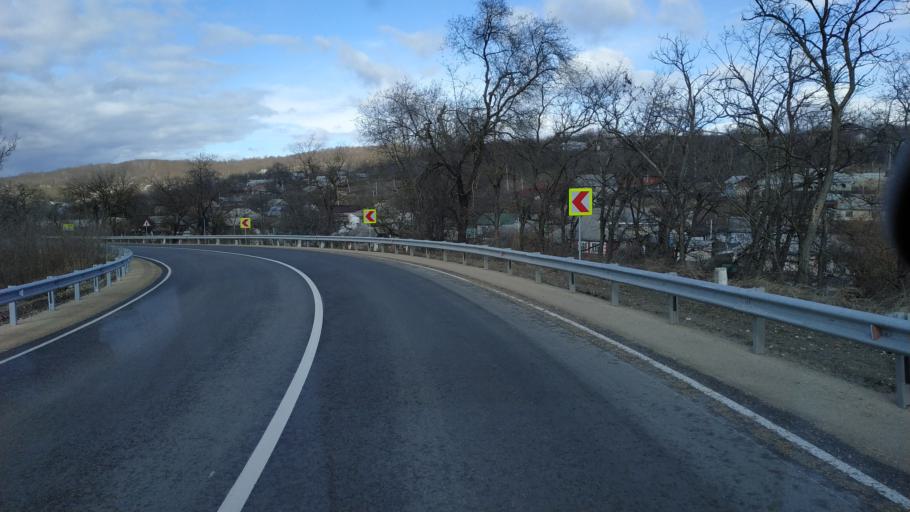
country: MD
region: Stinga Nistrului
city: Bucovat
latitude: 47.1854
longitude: 28.4667
